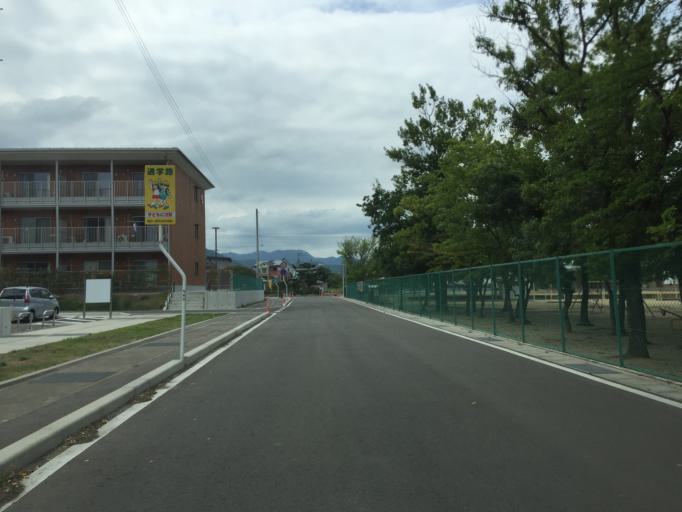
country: JP
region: Fukushima
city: Fukushima-shi
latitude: 37.7850
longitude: 140.4311
